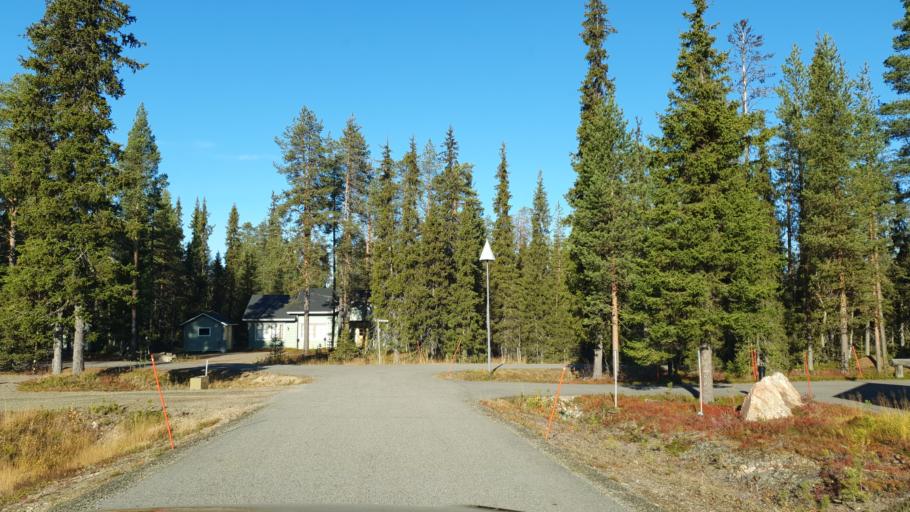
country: FI
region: Lapland
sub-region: Tunturi-Lappi
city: Kolari
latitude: 67.5992
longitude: 24.1796
